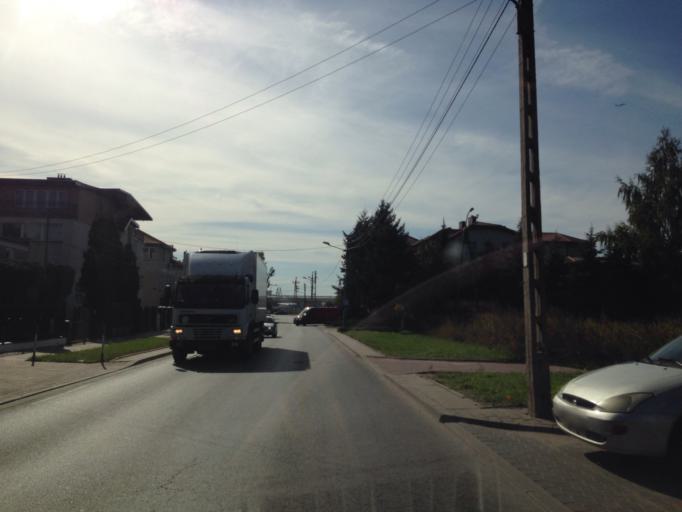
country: PL
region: Masovian Voivodeship
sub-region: Warszawa
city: Wlochy
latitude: 52.1879
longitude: 20.9433
